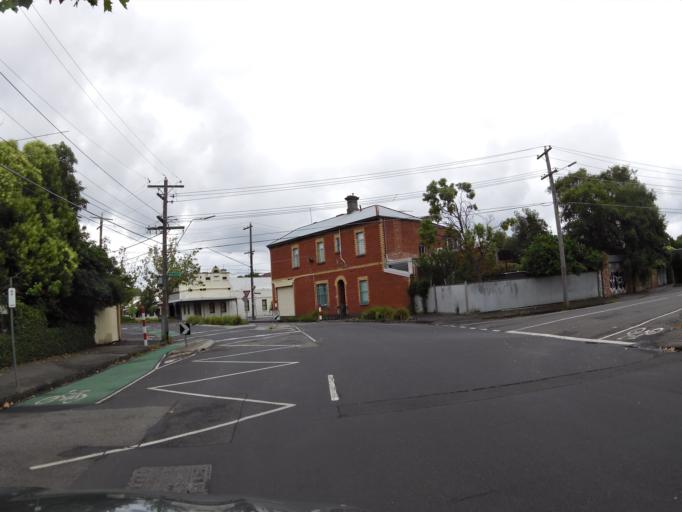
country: AU
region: Victoria
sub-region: Yarra
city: Clifton Hill
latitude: -37.7883
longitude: 145.0003
